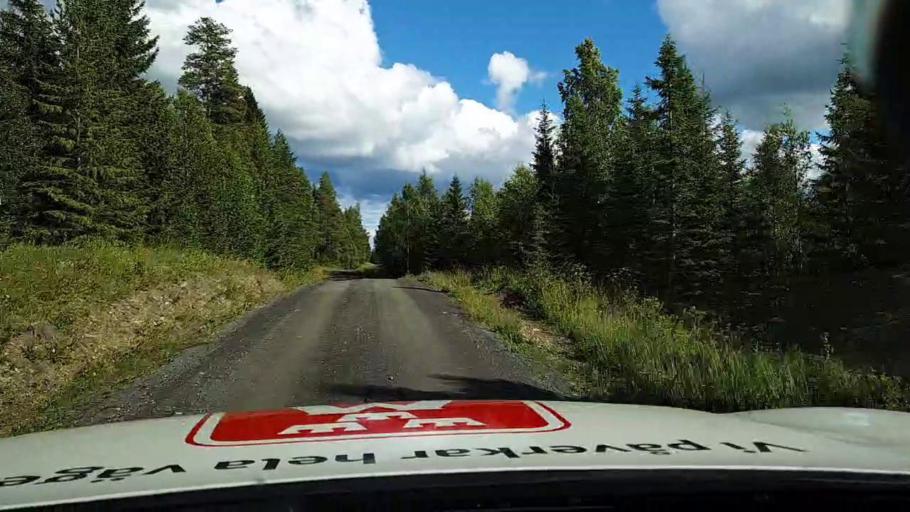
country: SE
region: Jaemtland
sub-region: Krokoms Kommun
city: Valla
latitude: 63.3262
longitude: 13.7395
